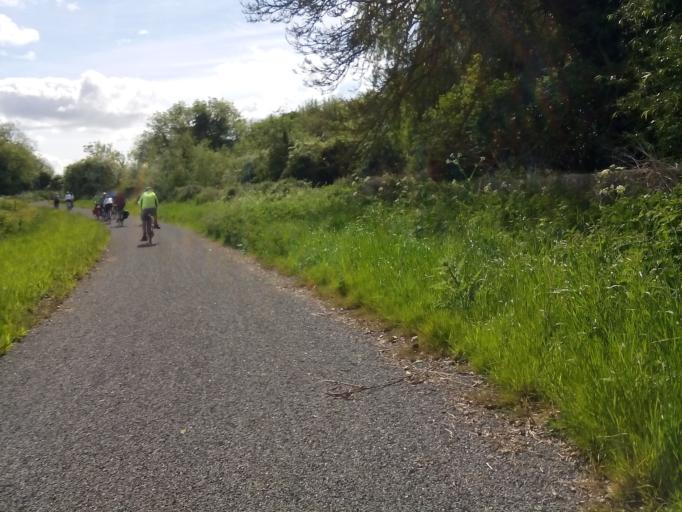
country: GB
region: England
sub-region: Cambridgeshire
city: Harston
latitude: 52.1557
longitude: 0.0903
